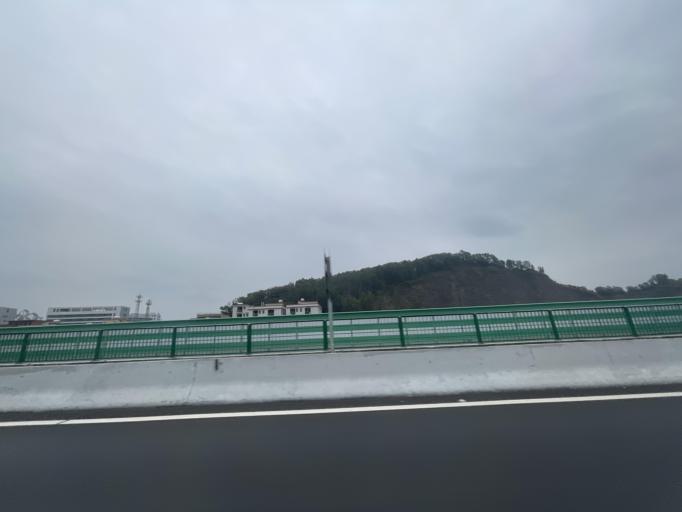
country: CN
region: Guangdong
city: Nansha
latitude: 22.7850
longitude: 113.5295
